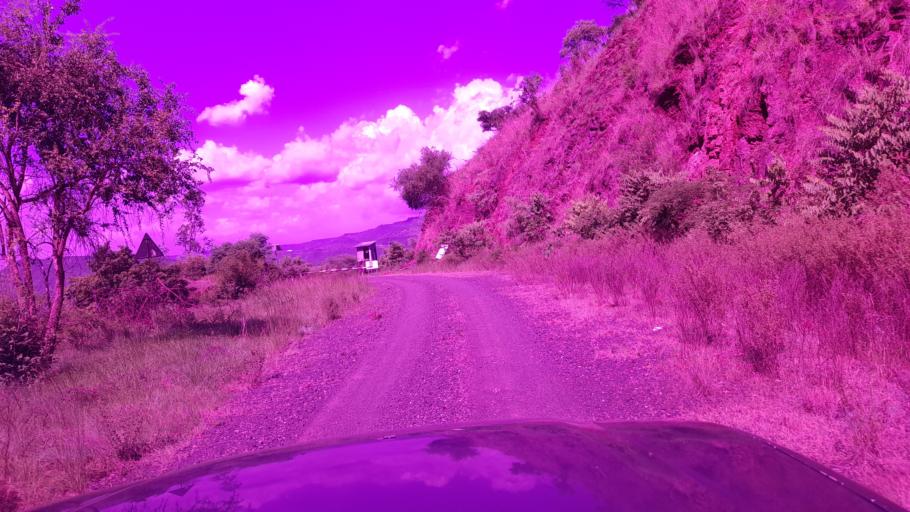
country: ET
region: Southern Nations, Nationalities, and People's Region
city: K'olito
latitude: 7.7726
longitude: 37.5551
